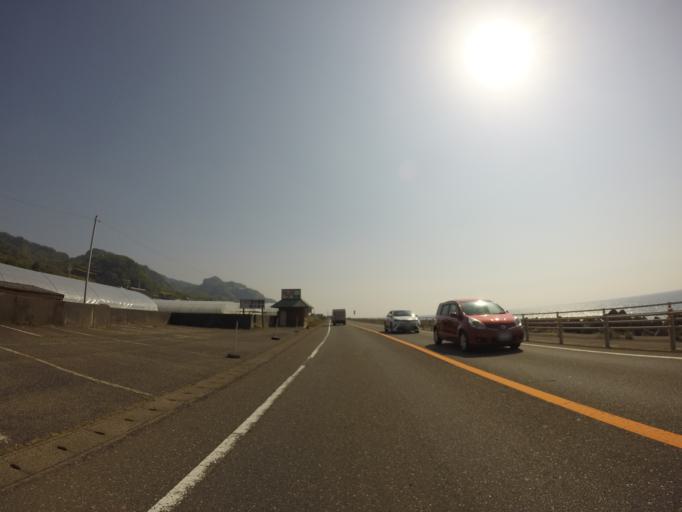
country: JP
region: Shizuoka
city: Shizuoka-shi
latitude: 34.9552
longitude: 138.4547
